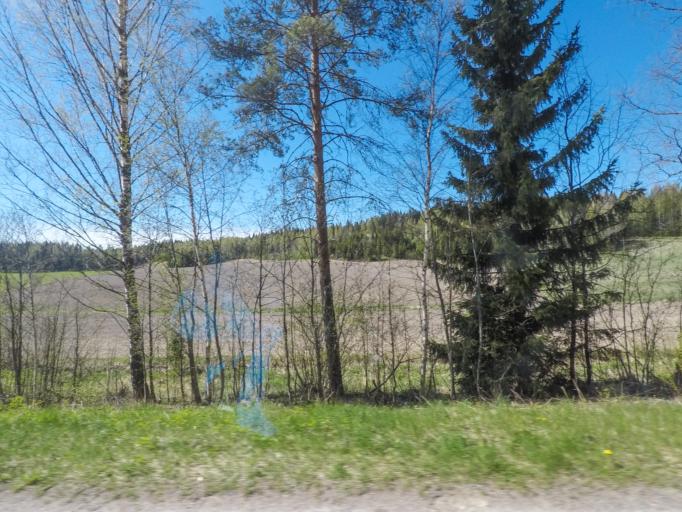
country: FI
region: Uusimaa
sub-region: Helsinki
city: Sammatti
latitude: 60.4058
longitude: 23.8183
